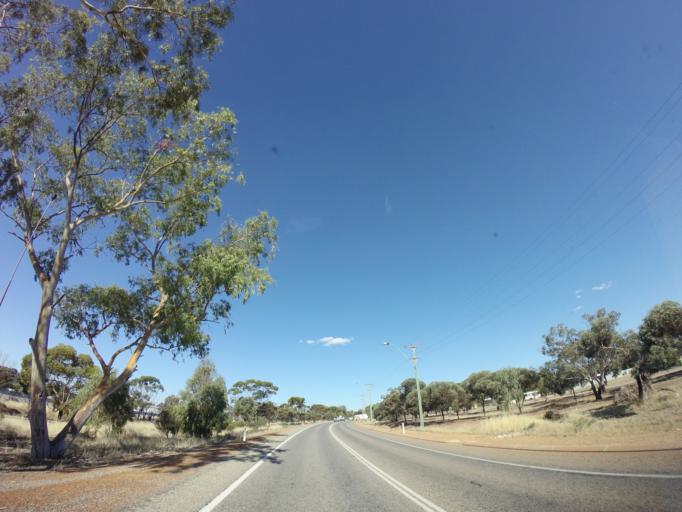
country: AU
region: Western Australia
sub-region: Merredin
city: Merredin
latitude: -31.4817
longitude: 118.2627
